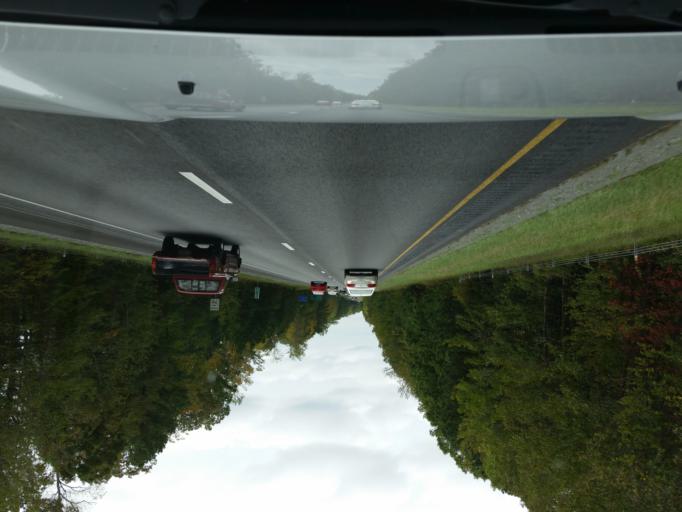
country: US
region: Virginia
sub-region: New Kent County
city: New Kent
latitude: 37.5017
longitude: -77.0713
